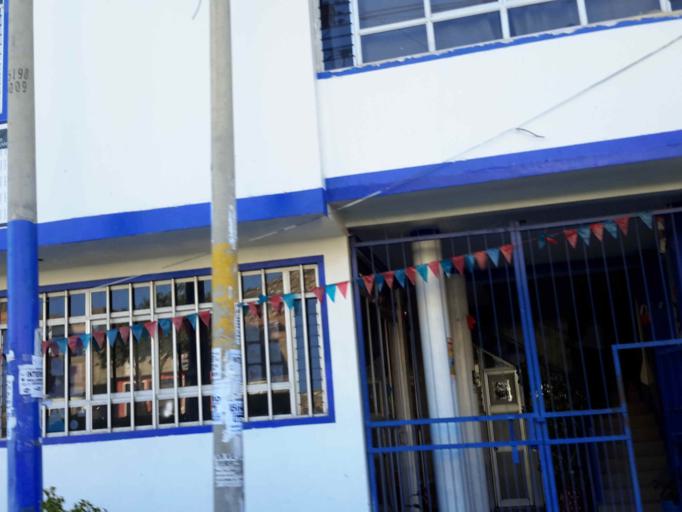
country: PE
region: Ayacucho
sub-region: Provincia de Huamanga
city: Ayacucho
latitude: -13.1409
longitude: -74.2285
